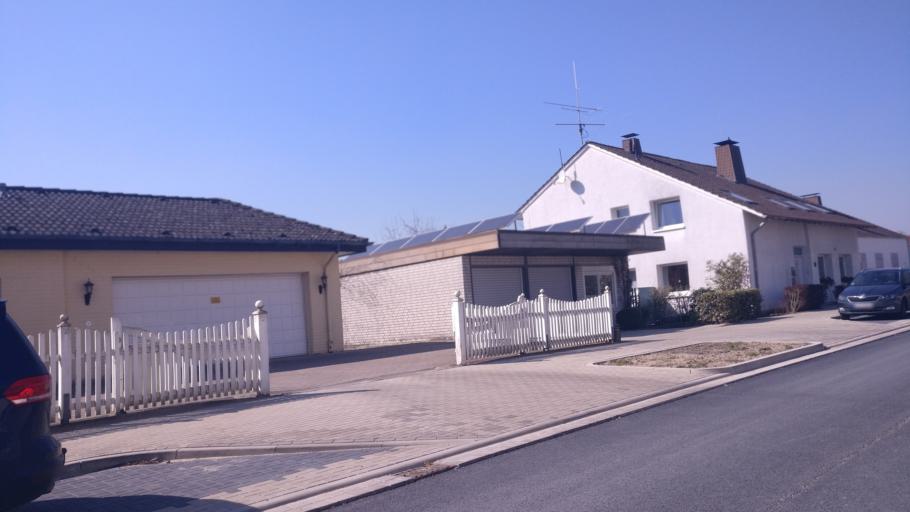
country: DE
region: North Rhine-Westphalia
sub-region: Regierungsbezirk Detmold
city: Lage
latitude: 51.9919
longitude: 8.7848
